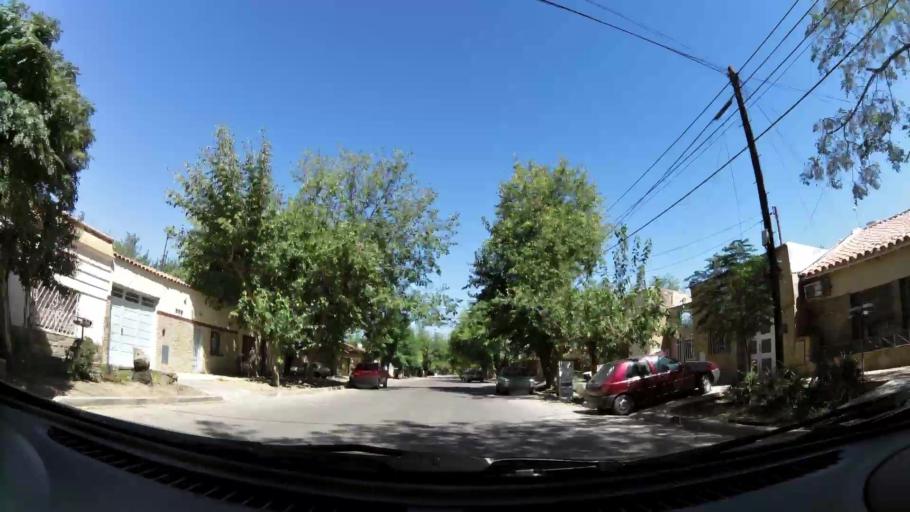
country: AR
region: Mendoza
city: Mendoza
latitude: -32.8771
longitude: -68.8208
